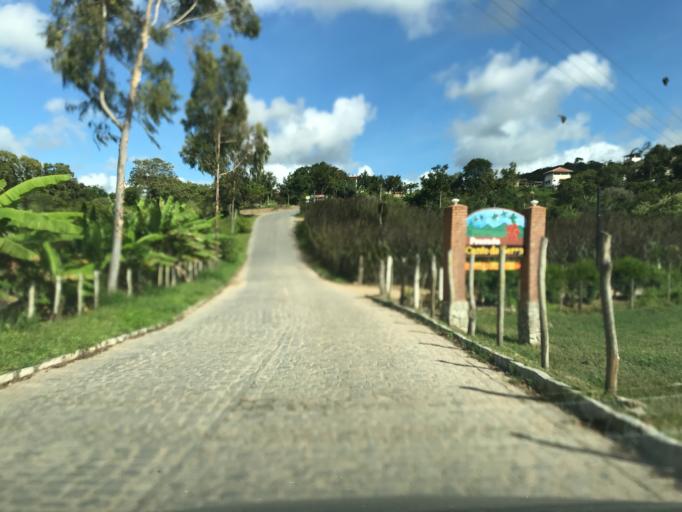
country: BR
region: Pernambuco
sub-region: Bezerros
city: Bezerros
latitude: -8.1751
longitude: -35.7694
